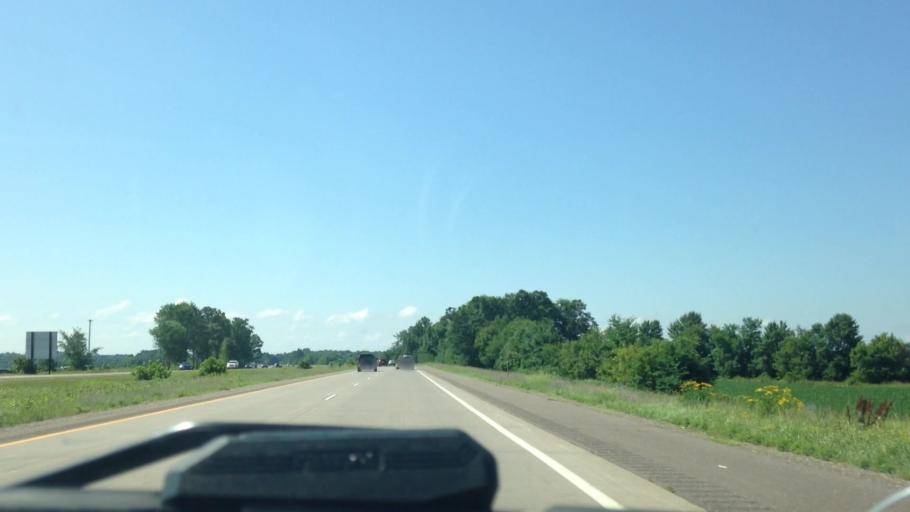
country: US
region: Wisconsin
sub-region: Barron County
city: Rice Lake
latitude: 45.4612
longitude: -91.7588
